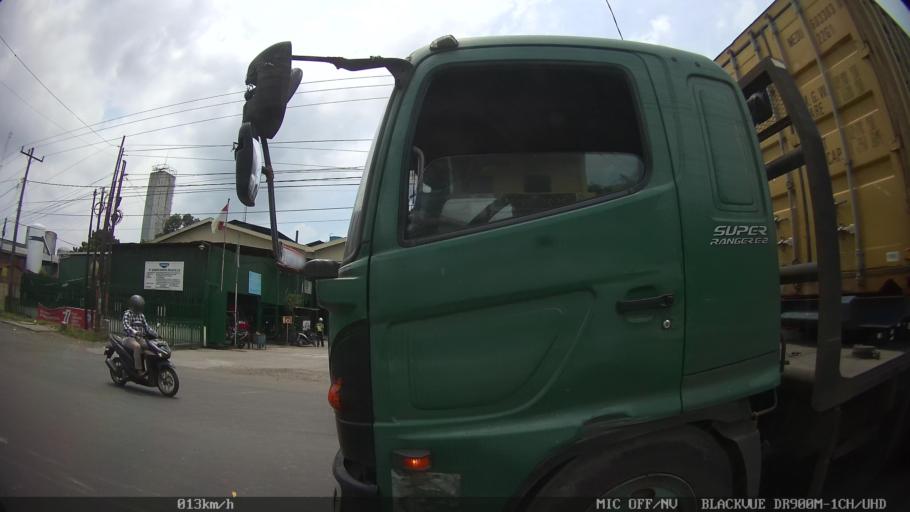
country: ID
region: North Sumatra
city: Labuhan Deli
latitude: 3.6672
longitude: 98.6670
